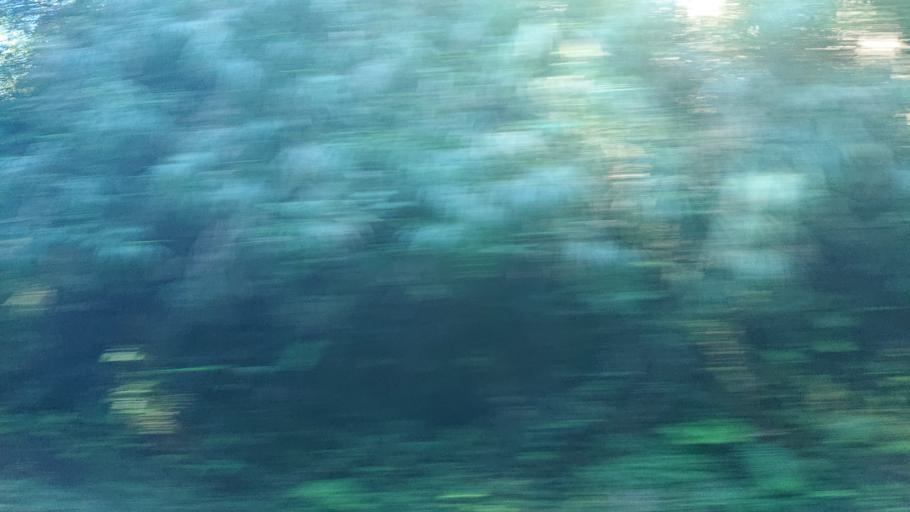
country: TW
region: Taiwan
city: Lugu
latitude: 23.4985
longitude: 120.7952
